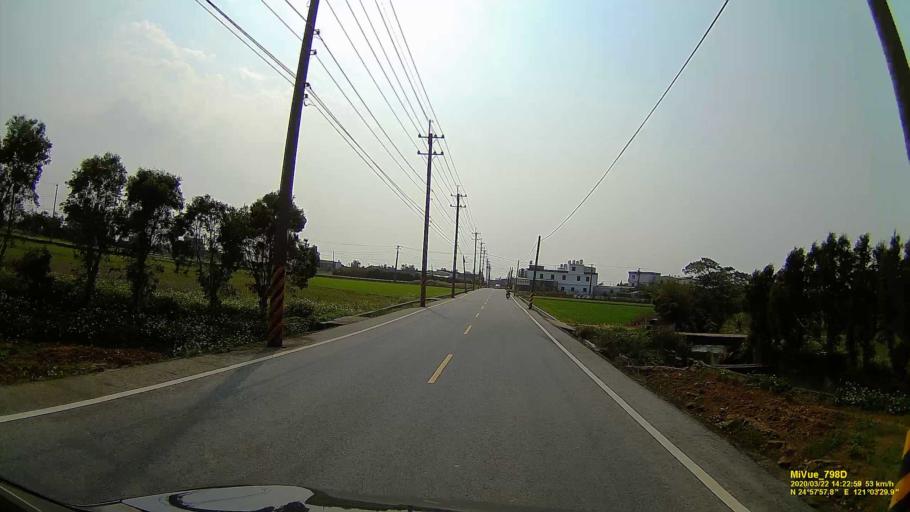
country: TW
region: Taiwan
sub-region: Hsinchu
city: Zhubei
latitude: 24.9660
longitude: 121.0581
